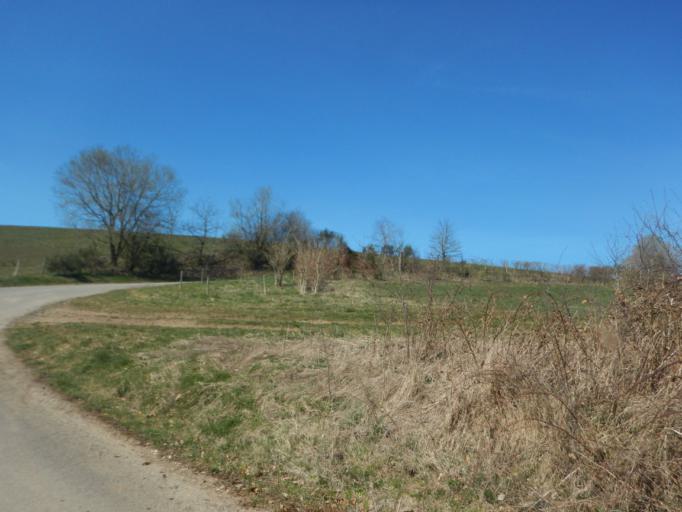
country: LU
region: Diekirch
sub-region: Canton de Clervaux
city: Weiswampach
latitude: 50.1165
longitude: 6.0484
